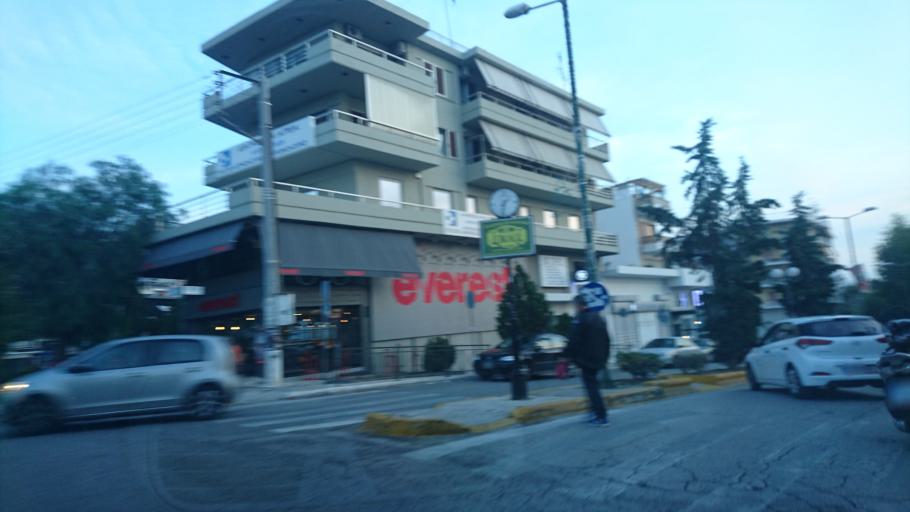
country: GR
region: Attica
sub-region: Nomarchia Athinas
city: Ilioupoli
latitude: 37.9315
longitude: 23.7558
